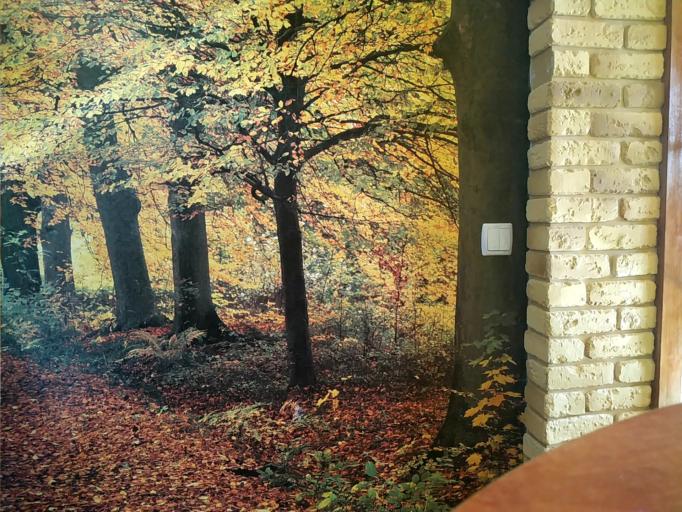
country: RU
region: Jaroslavl
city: Kukoboy
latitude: 58.8272
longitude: 39.7584
